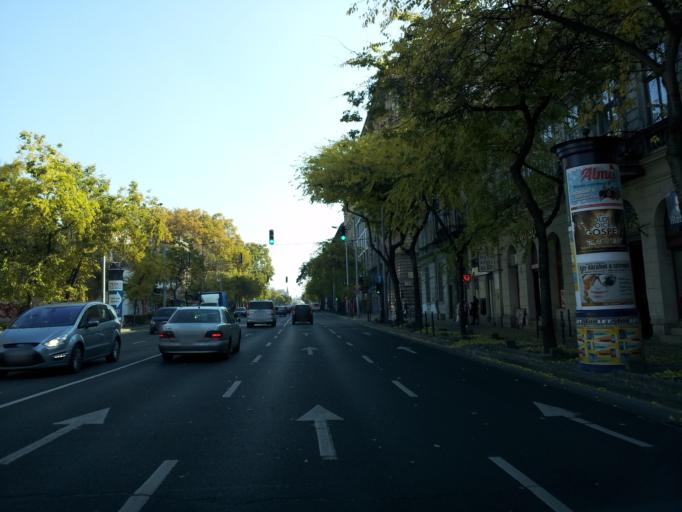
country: HU
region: Budapest
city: Budapest VIII. keruelet
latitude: 47.4829
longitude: 19.0781
